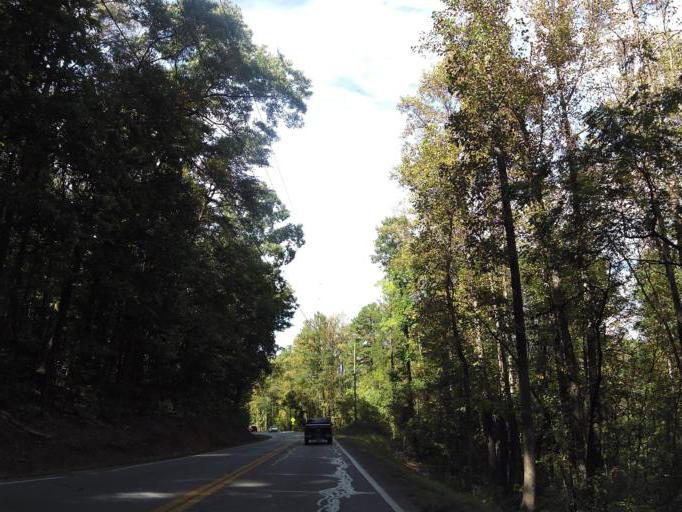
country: US
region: Georgia
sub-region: Pickens County
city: Nelson
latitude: 34.4186
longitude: -84.3215
